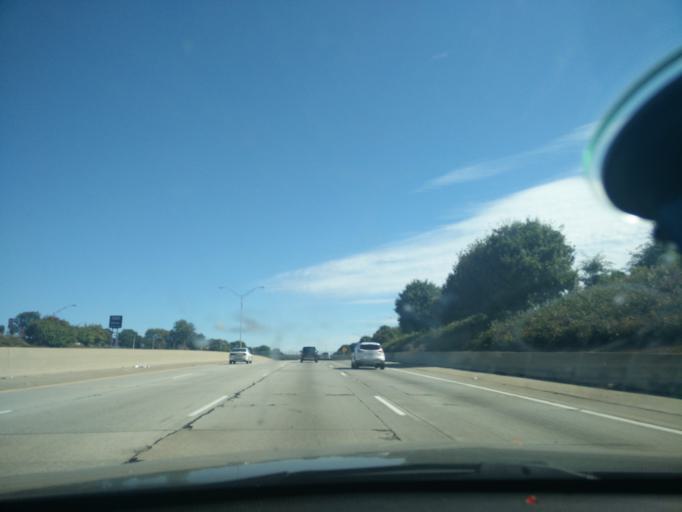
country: US
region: Michigan
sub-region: Macomb County
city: Center Line
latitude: 42.4916
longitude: -83.0263
